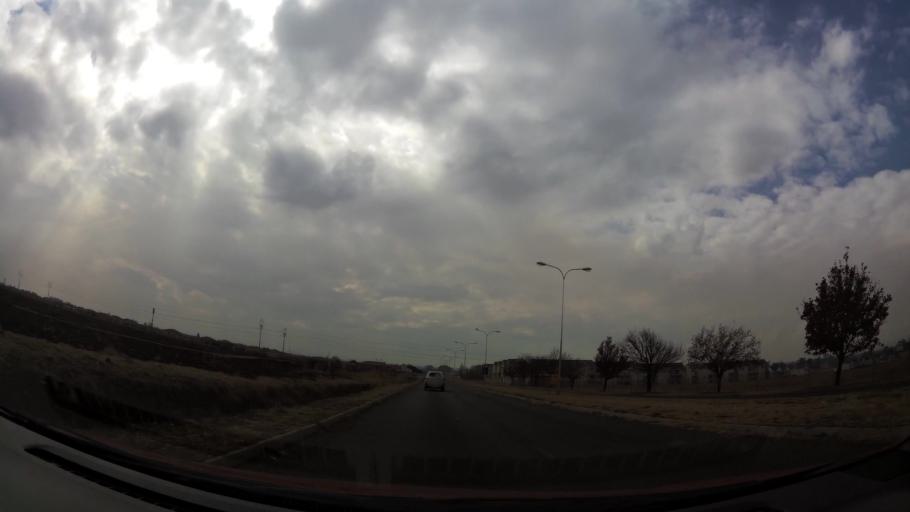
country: ZA
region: Gauteng
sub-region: Sedibeng District Municipality
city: Vanderbijlpark
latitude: -26.7199
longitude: 27.8833
